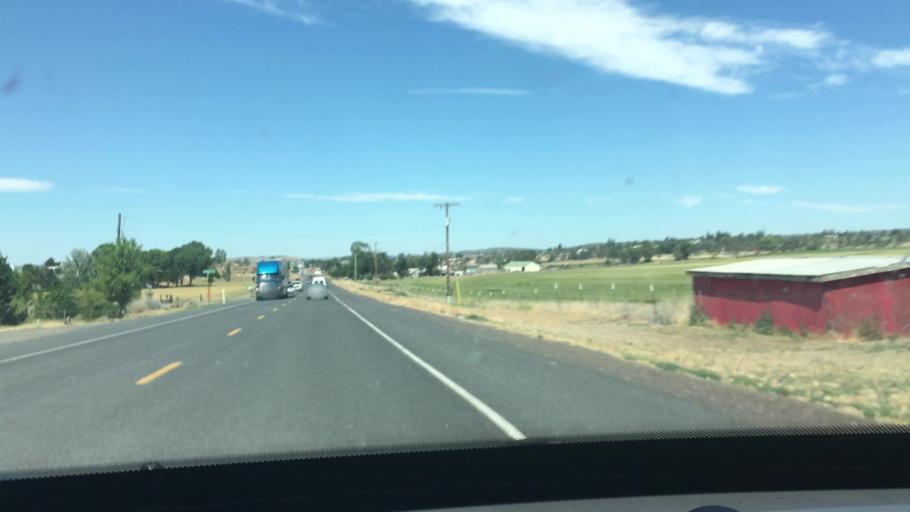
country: US
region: Oregon
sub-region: Jefferson County
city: Madras
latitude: 44.5966
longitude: -121.1454
